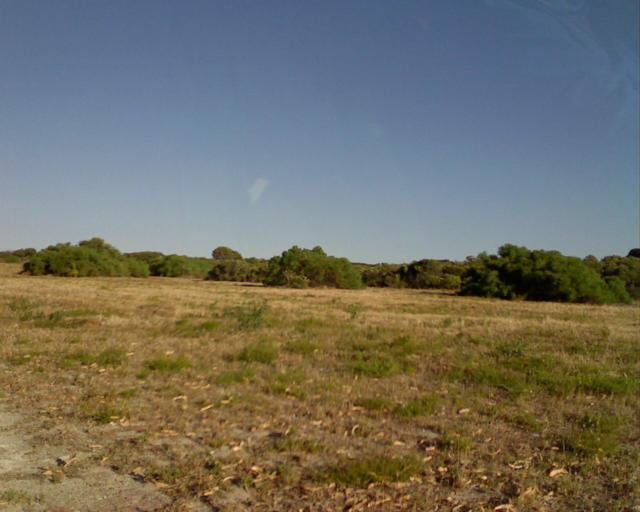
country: AU
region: Western Australia
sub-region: Dandaragan
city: Jurien Bay
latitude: -30.0509
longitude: 114.9763
